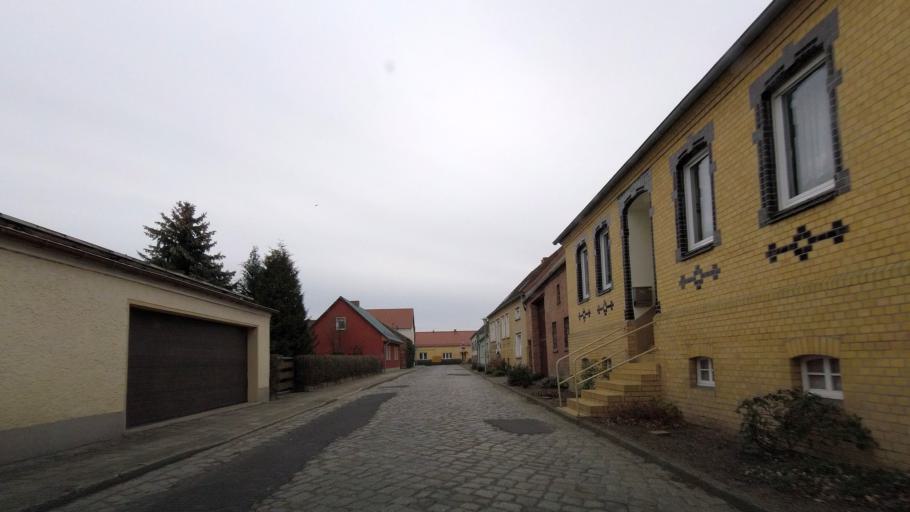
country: DE
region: Brandenburg
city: Treuenbrietzen
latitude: 52.0721
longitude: 12.9400
